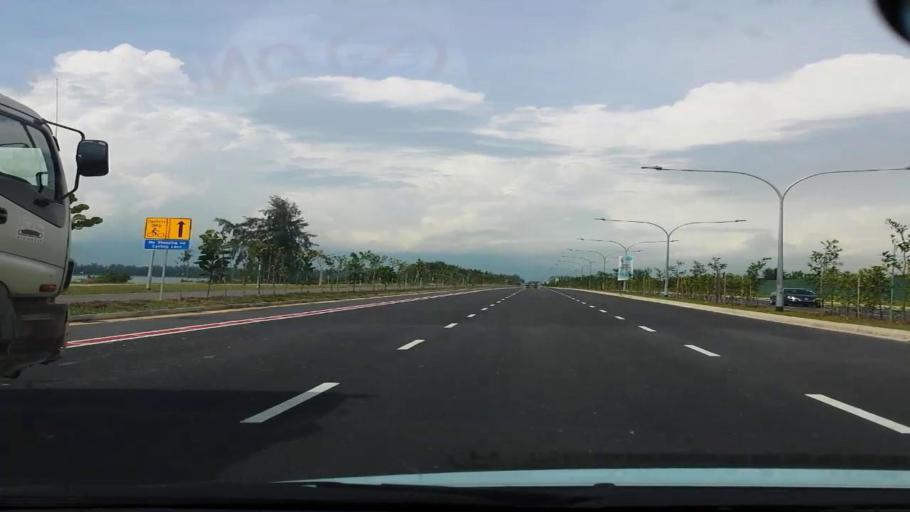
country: SG
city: Singapore
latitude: 1.3463
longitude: 104.0276
